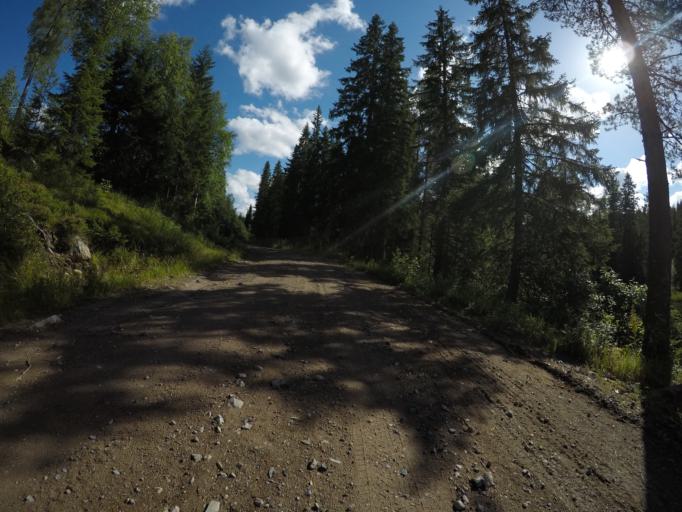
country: SE
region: Dalarna
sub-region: Ludvika Kommun
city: Abborrberget
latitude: 60.0096
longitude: 14.6097
